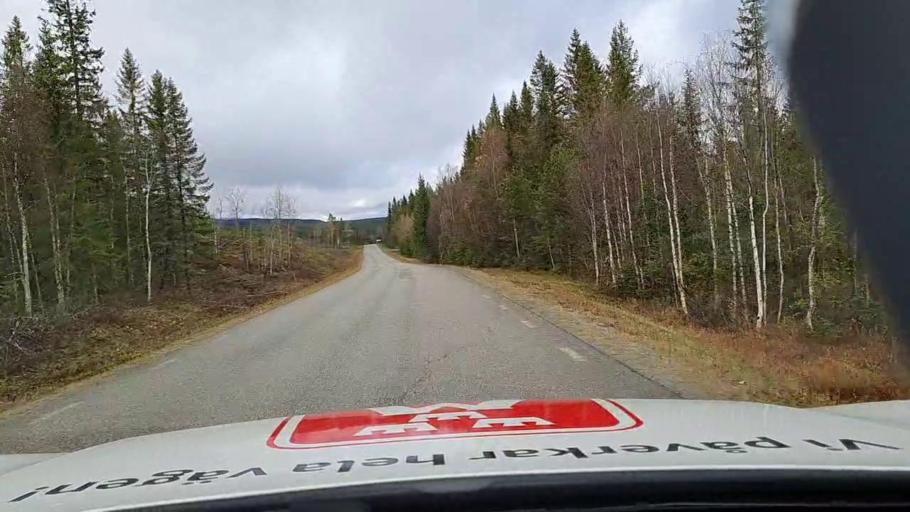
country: SE
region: Jaemtland
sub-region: Bergs Kommun
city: Hoverberg
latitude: 63.0395
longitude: 14.0165
